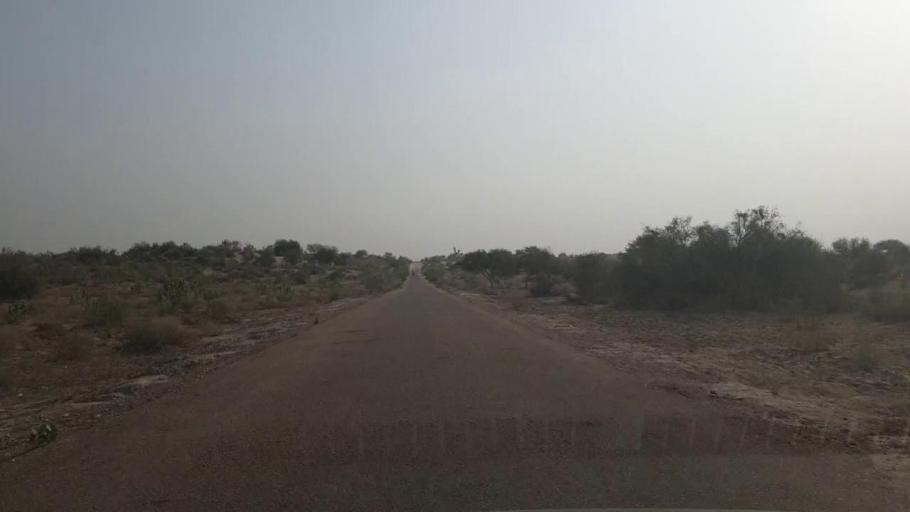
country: PK
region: Sindh
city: Chor
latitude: 25.4635
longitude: 69.9670
